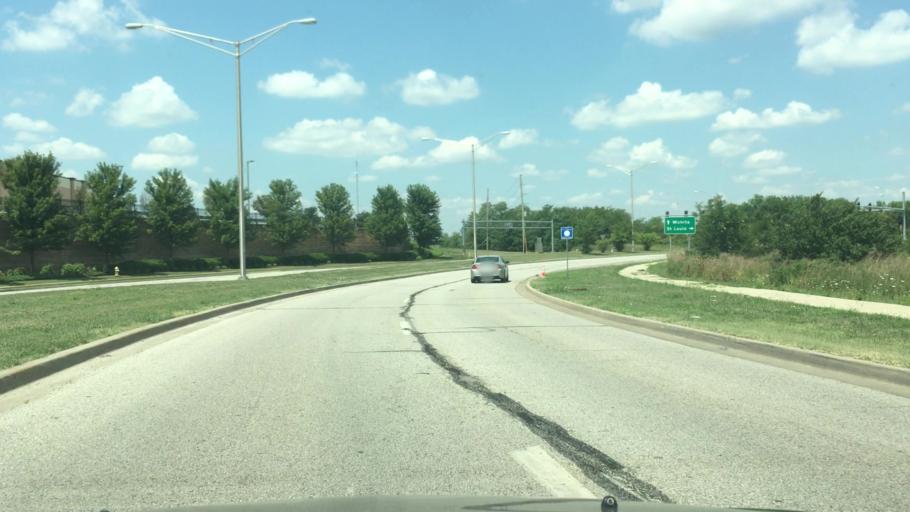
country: US
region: Missouri
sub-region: Jackson County
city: Lees Summit
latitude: 38.9334
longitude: -94.4010
